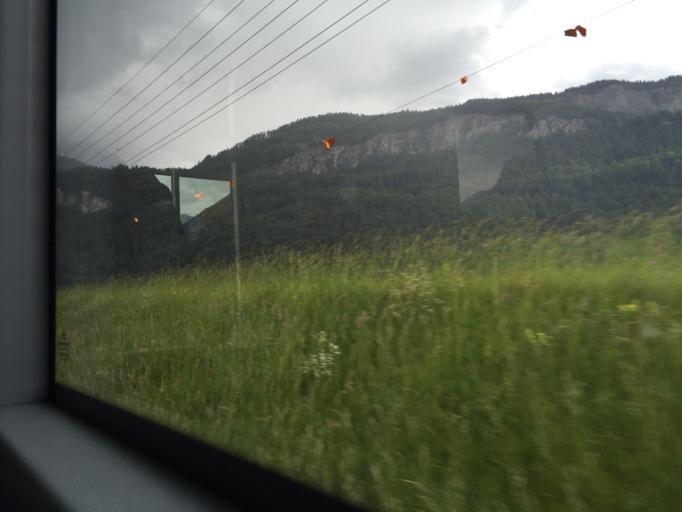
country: CH
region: Bern
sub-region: Interlaken-Oberhasli District
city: Meiringen
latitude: 46.7386
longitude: 8.1512
